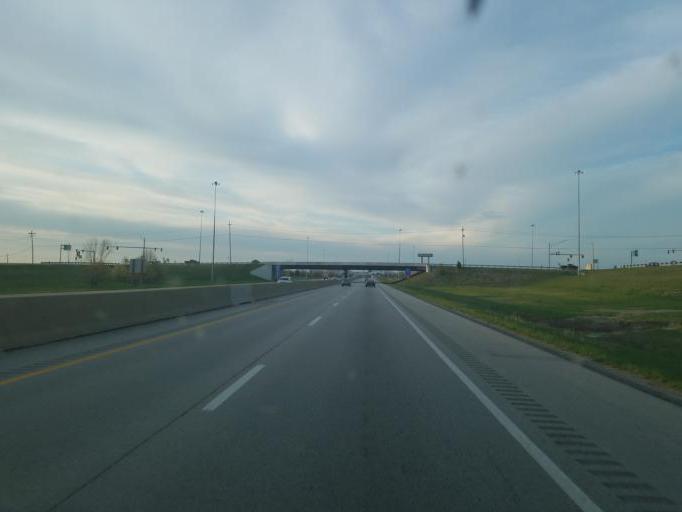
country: US
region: Ohio
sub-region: Wood County
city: Northwood
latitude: 41.6144
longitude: -83.4769
